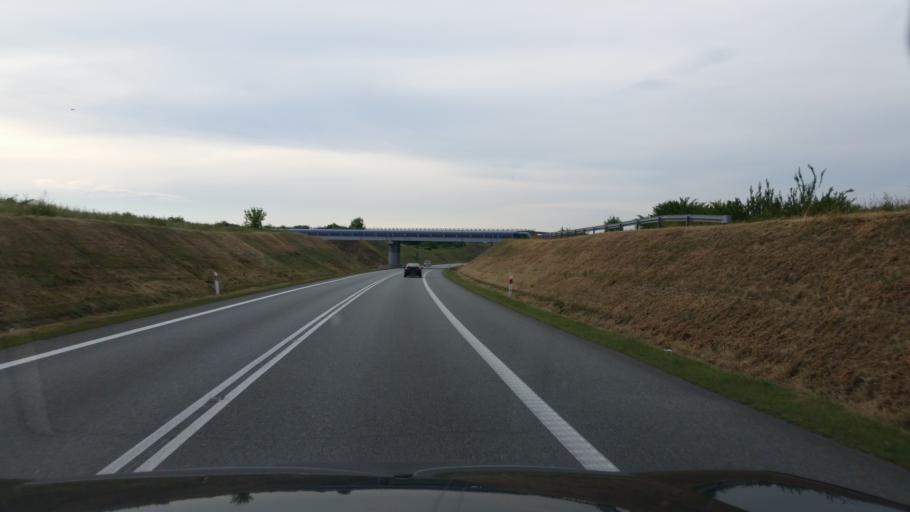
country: PL
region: Silesian Voivodeship
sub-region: Powiat bedzinski
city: Mierzecice
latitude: 50.4293
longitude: 19.1551
